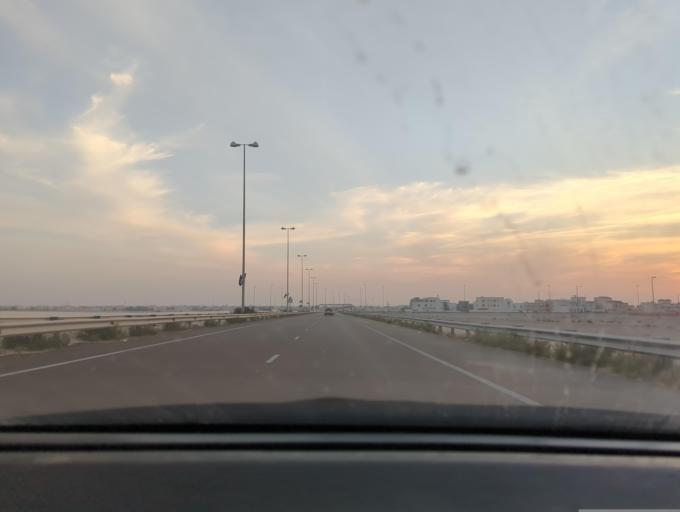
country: AE
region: Abu Dhabi
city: Abu Dhabi
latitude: 24.3348
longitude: 54.6508
